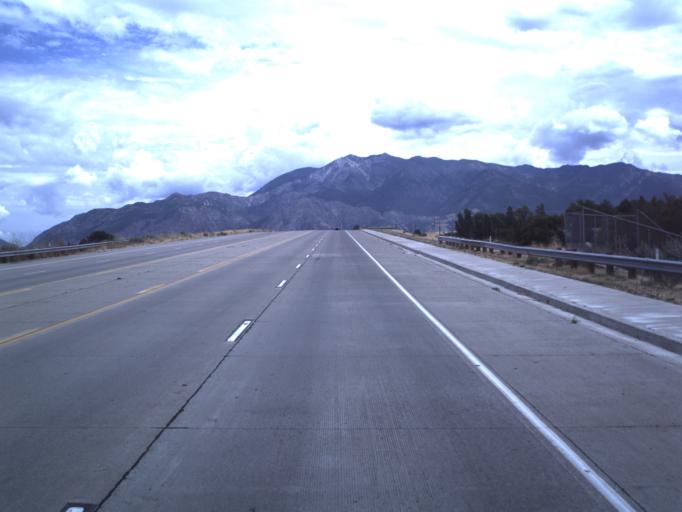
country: US
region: Utah
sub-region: Weber County
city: West Haven
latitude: 41.1977
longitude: -112.0300
